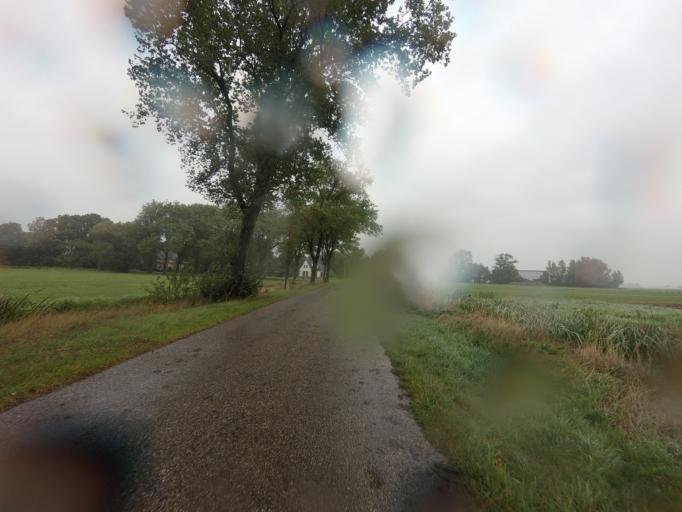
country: NL
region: Friesland
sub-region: Gemeente Boarnsterhim
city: Aldeboarn
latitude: 53.0618
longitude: 5.9166
